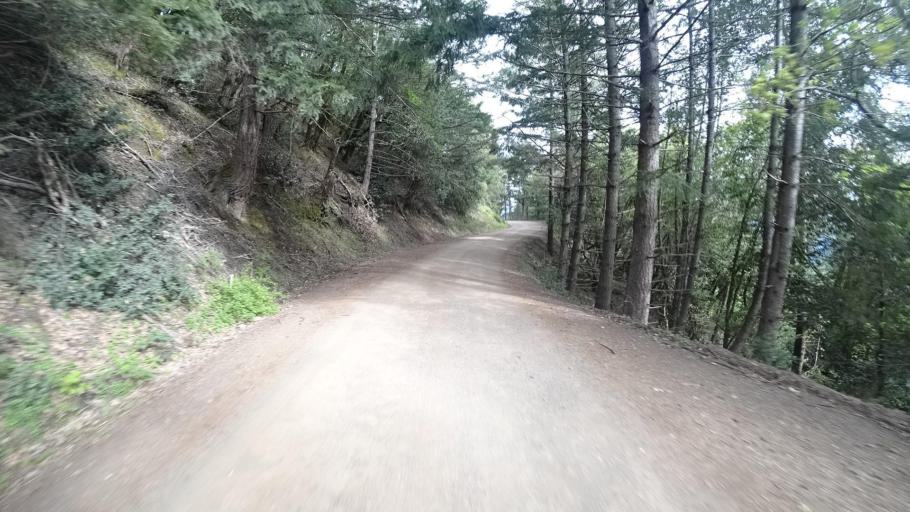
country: US
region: California
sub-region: Humboldt County
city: Redway
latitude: 40.2046
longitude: -123.7169
